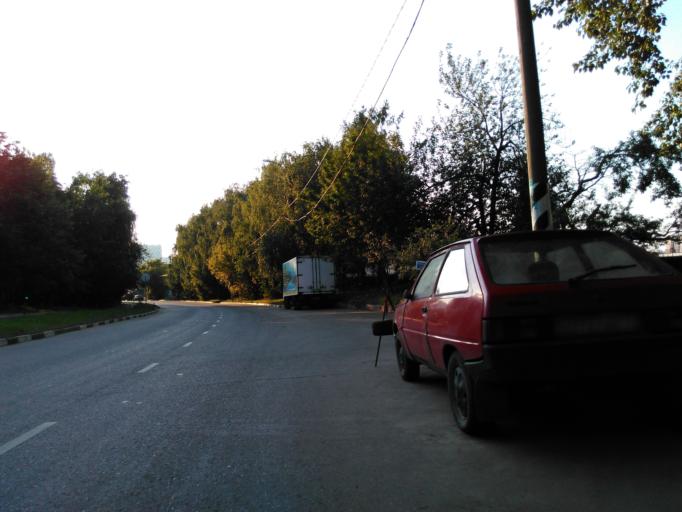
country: RU
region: Moskovskaya
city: Cheremushki
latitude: 55.6573
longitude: 37.5541
